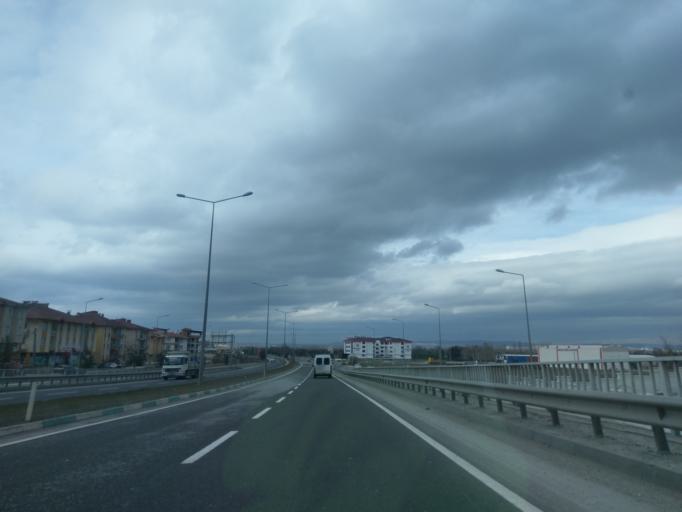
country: TR
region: Kuetahya
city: Kutahya
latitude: 39.4067
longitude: 30.0270
